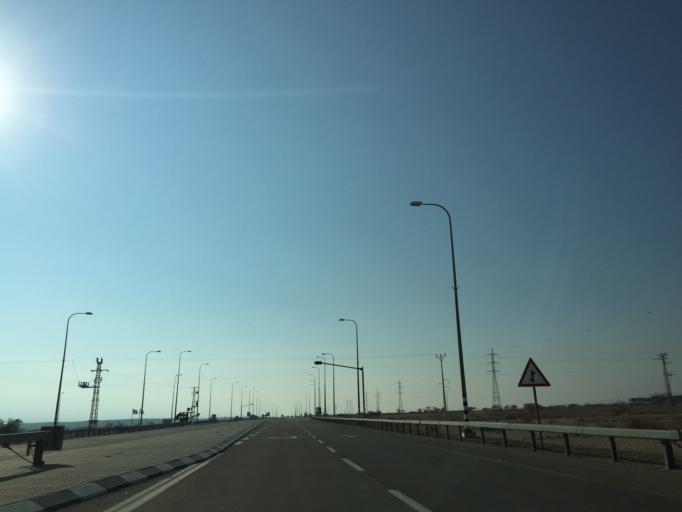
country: JO
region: Ma'an
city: Al Quwayrah
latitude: 29.8357
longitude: 35.0287
